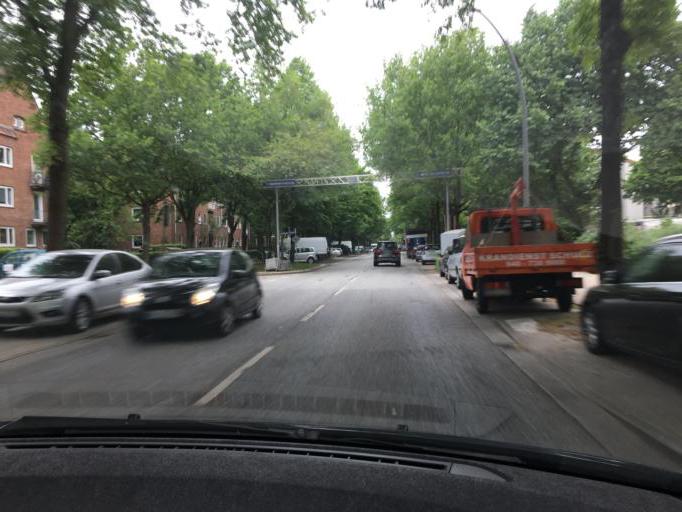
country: DE
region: Hamburg
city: Kleiner Grasbrook
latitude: 53.5074
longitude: 9.9924
